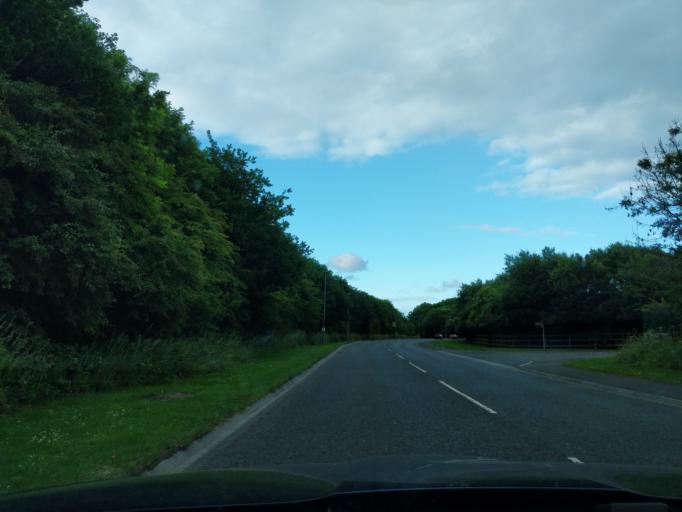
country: GB
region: England
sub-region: Northumberland
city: Seaton Delaval
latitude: 55.0804
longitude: -1.5304
